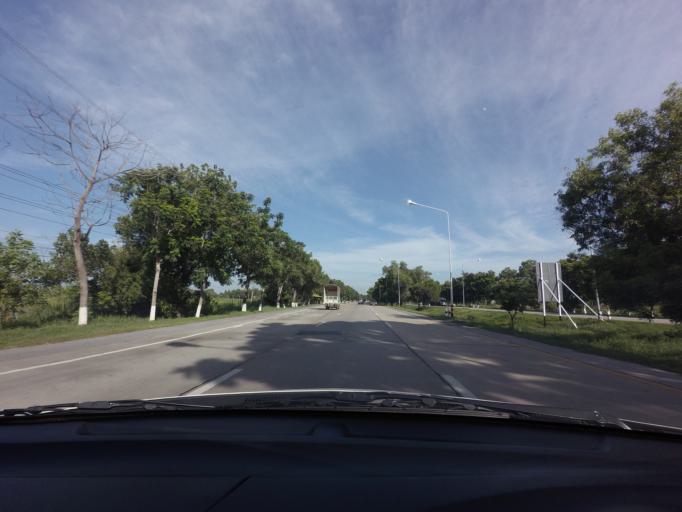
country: TH
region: Suphan Buri
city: Bang Pla Ma
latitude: 14.3890
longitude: 100.1738
